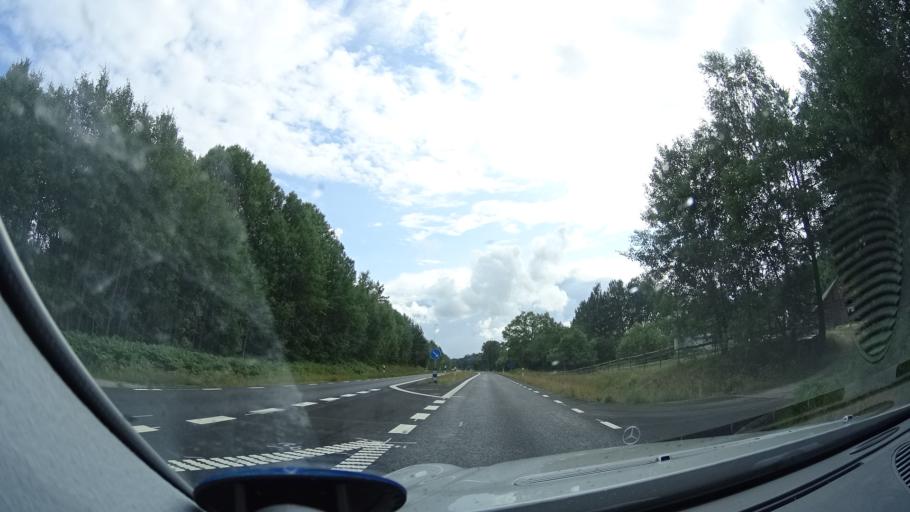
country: SE
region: Blekinge
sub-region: Karlshamns Kommun
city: Svangsta
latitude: 56.2280
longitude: 14.8217
